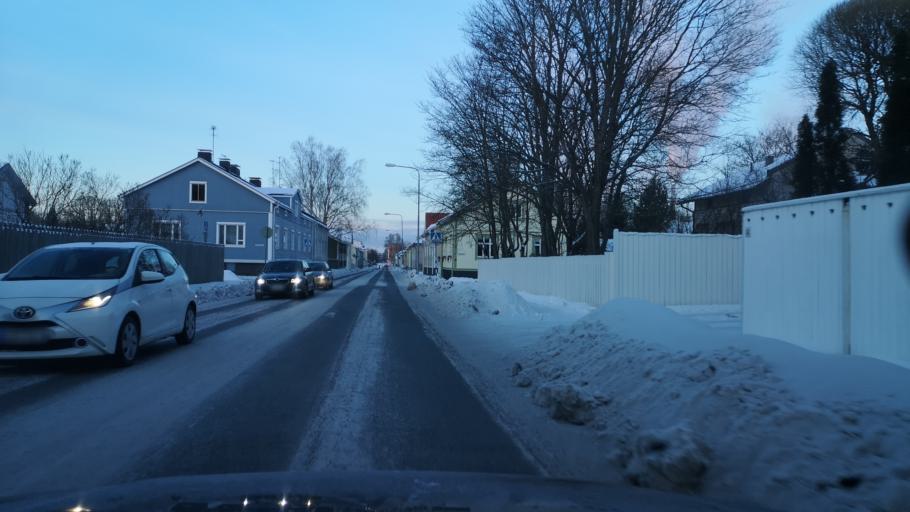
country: FI
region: Satakunta
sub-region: Pori
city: Pori
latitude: 61.4810
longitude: 21.8059
